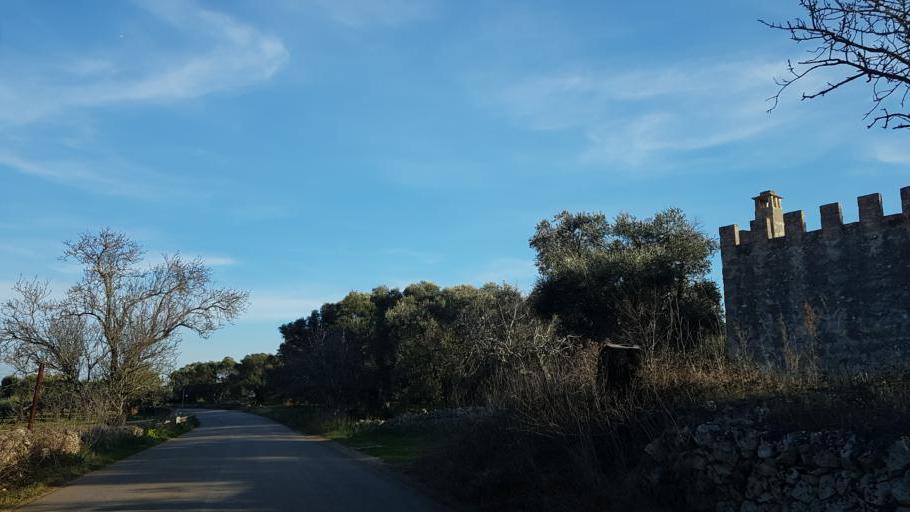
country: IT
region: Apulia
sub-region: Provincia di Brindisi
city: San Vito dei Normanni
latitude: 40.7010
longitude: 17.7287
